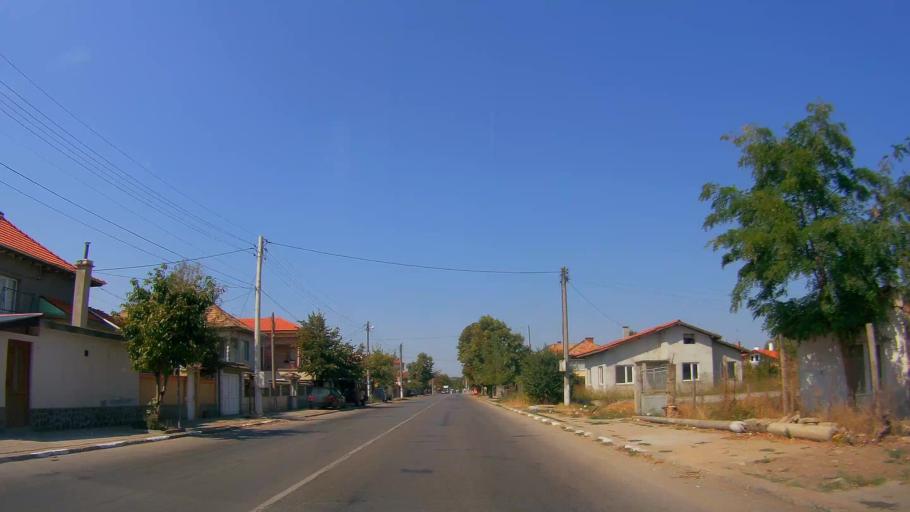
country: BG
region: Razgrad
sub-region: Obshtina Tsar Kaloyan
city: Tsar Kaloyan
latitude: 43.6048
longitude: 26.2416
